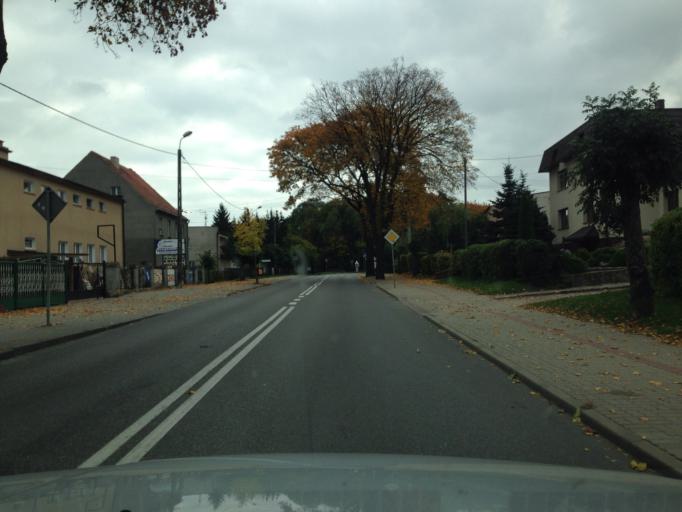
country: PL
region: Warmian-Masurian Voivodeship
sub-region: Powiat ilawski
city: Lubawa
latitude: 53.5003
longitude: 19.7550
